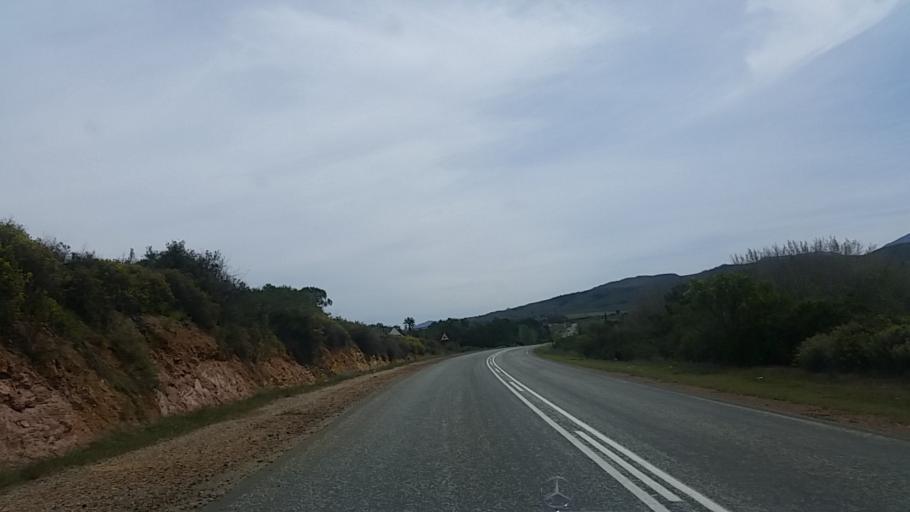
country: ZA
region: Western Cape
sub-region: Eden District Municipality
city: Knysna
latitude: -33.7739
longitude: 22.9027
